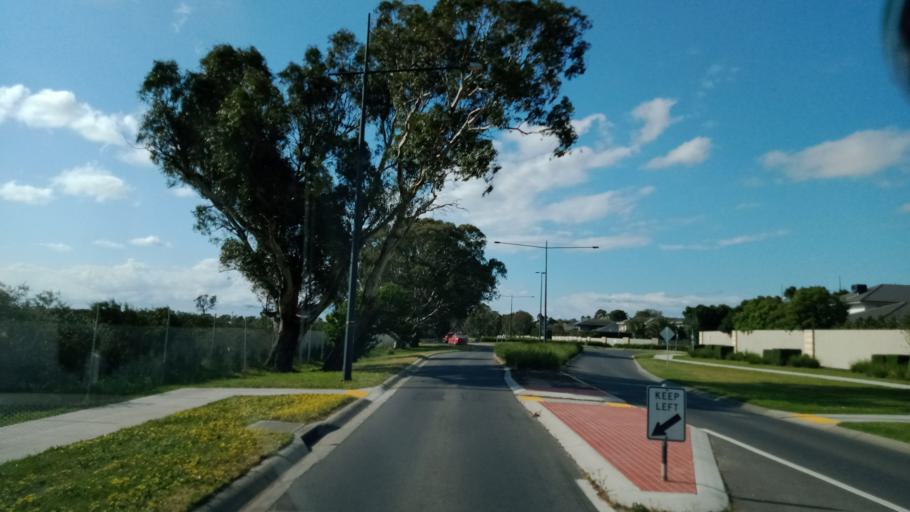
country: AU
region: Victoria
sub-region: Frankston
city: Sandhurst
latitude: -38.0814
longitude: 145.2014
